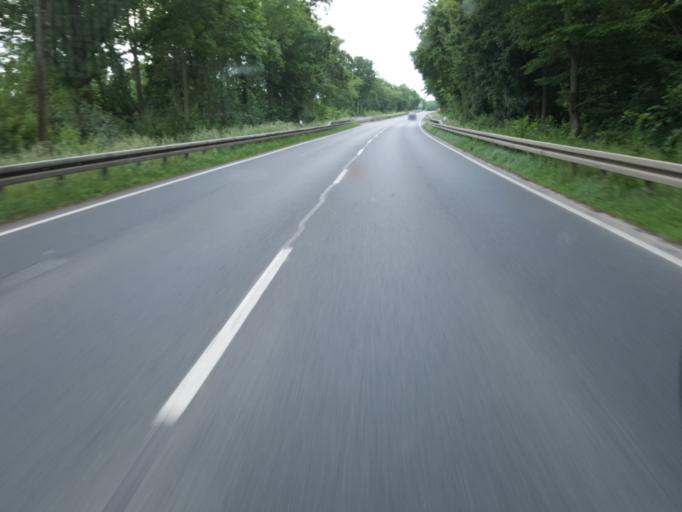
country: DE
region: Lower Saxony
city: Stolzenau
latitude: 52.5080
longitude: 9.0695
